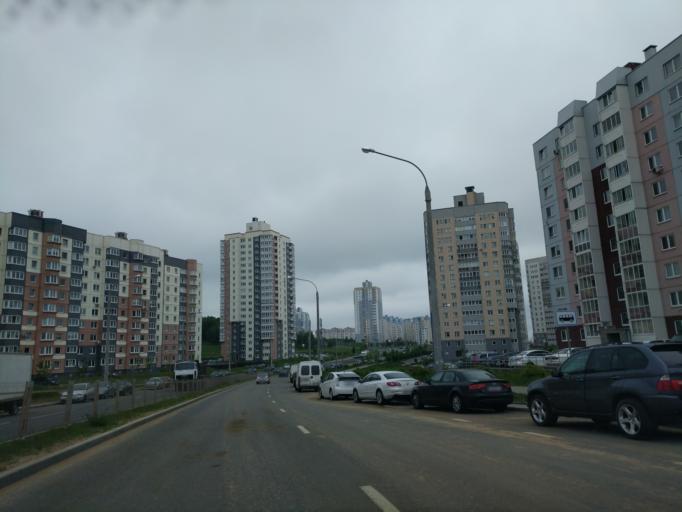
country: BY
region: Minsk
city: Novoye Medvezhino
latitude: 53.8767
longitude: 27.4433
